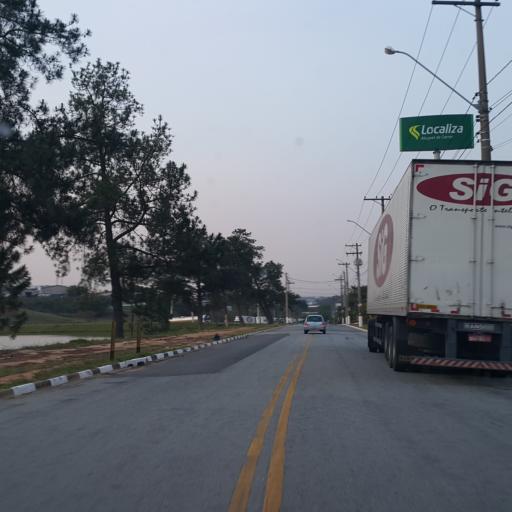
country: BR
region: Sao Paulo
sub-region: Vinhedo
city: Vinhedo
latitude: -23.0703
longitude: -47.0018
